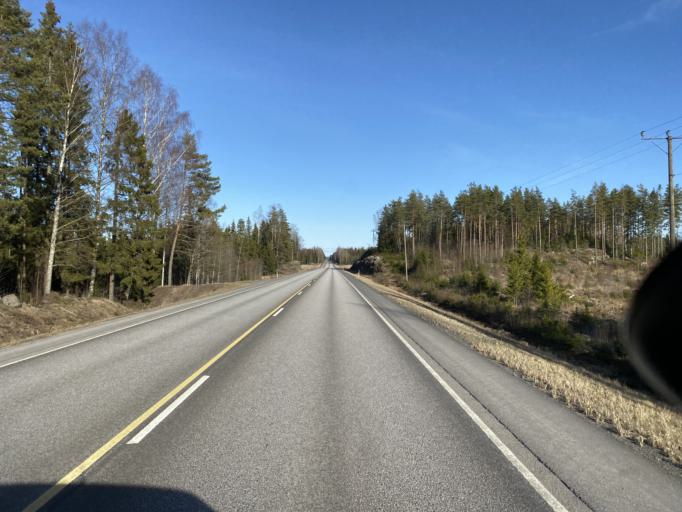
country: FI
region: Satakunta
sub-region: Rauma
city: Eura
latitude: 61.1312
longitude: 22.0374
